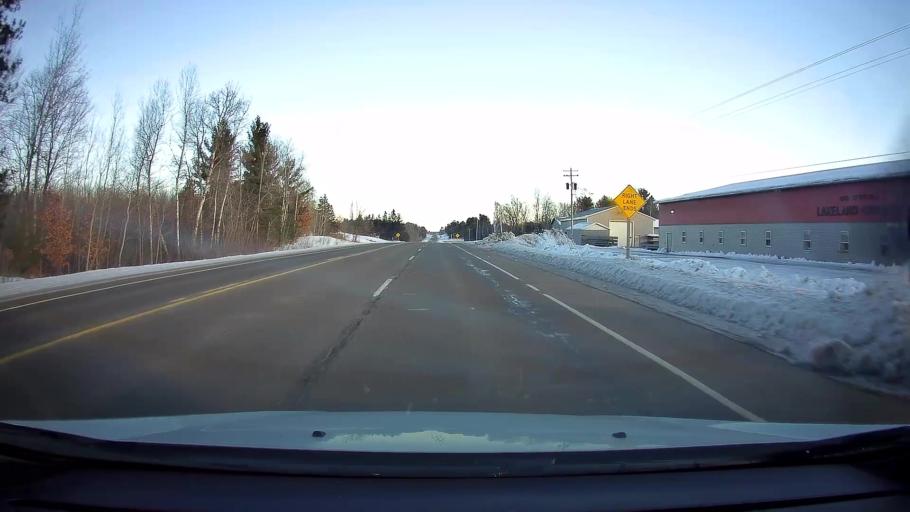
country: US
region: Wisconsin
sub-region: Barron County
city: Cumberland
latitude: 45.5724
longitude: -92.0174
